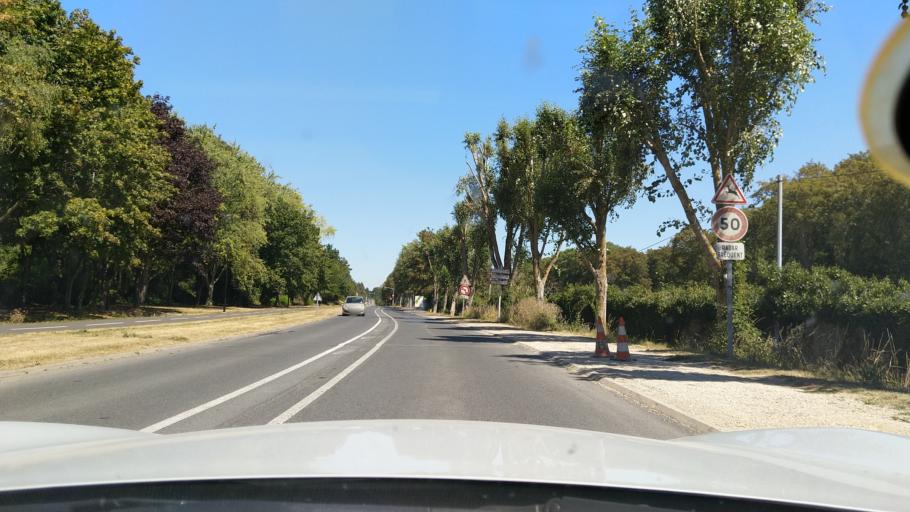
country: FR
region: Ile-de-France
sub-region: Departement de Seine-et-Marne
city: Lesigny
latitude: 48.7299
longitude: 2.6020
